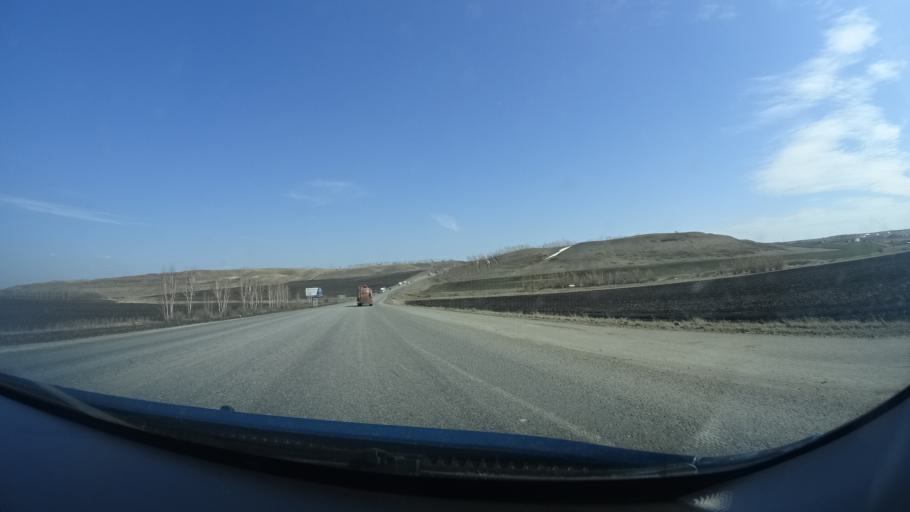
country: RU
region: Bashkortostan
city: Serafimovskiy
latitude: 54.4697
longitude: 53.7569
